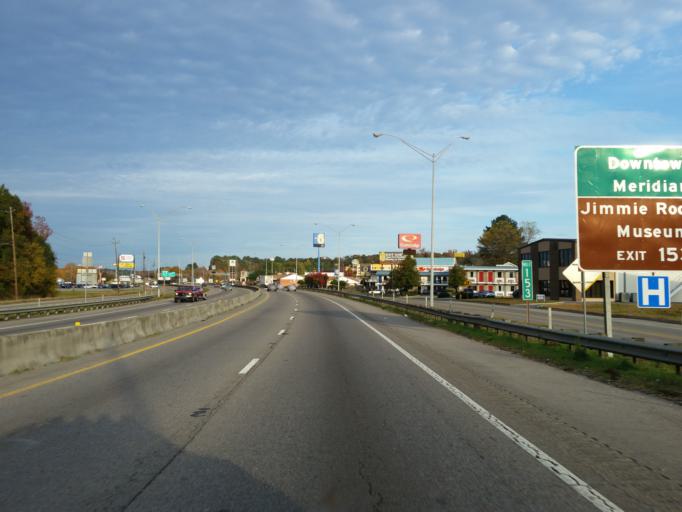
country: US
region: Mississippi
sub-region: Lauderdale County
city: Meridian
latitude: 32.3495
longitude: -88.6989
